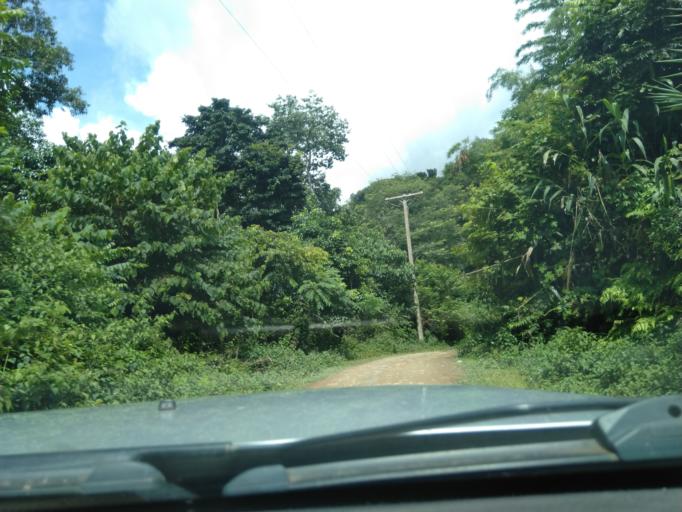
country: LA
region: Phongsali
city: Phongsali
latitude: 21.6976
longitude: 102.0769
